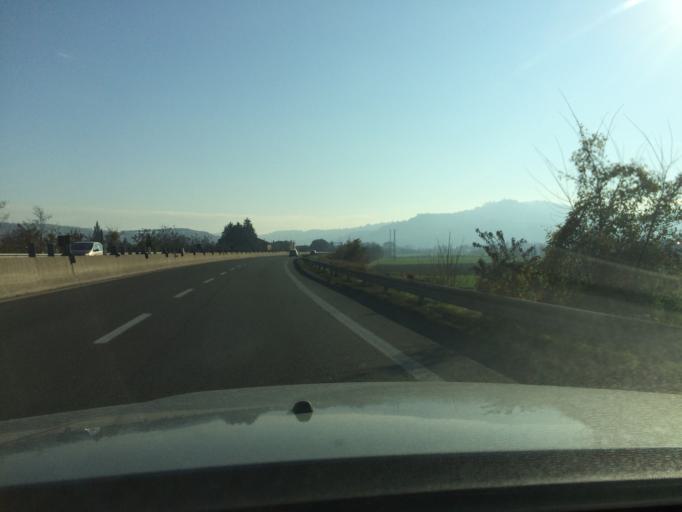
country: IT
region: Umbria
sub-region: Provincia di Perugia
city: Ponterio-Pian di Porto
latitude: 42.8141
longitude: 12.4045
